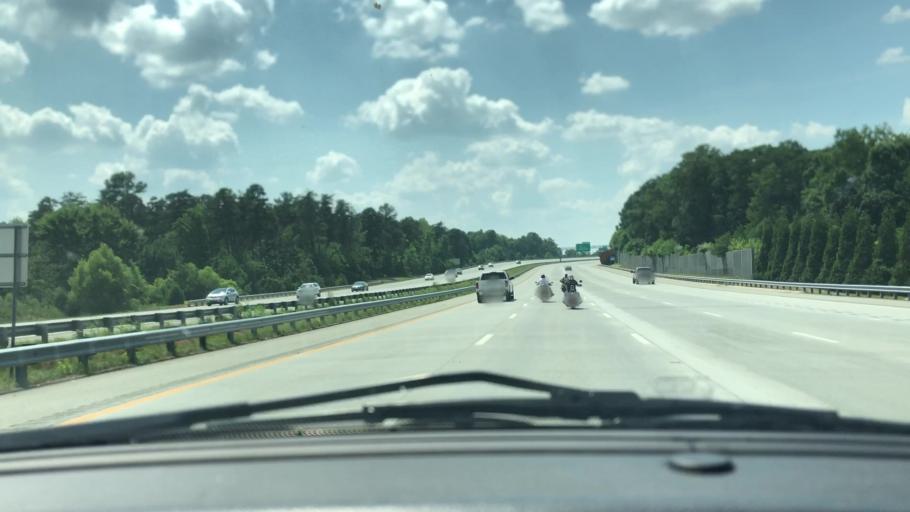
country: US
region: North Carolina
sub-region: Guilford County
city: Jamestown
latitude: 36.0457
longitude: -79.9046
